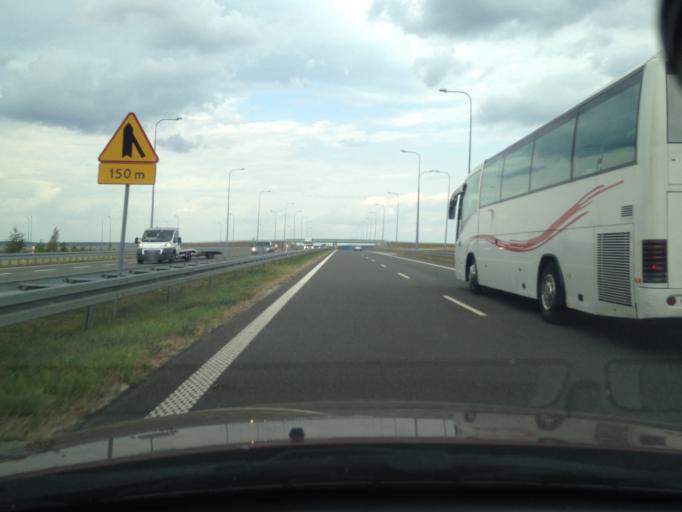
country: PL
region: West Pomeranian Voivodeship
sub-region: Powiat pyrzycki
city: Bielice
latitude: 53.1228
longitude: 14.7395
